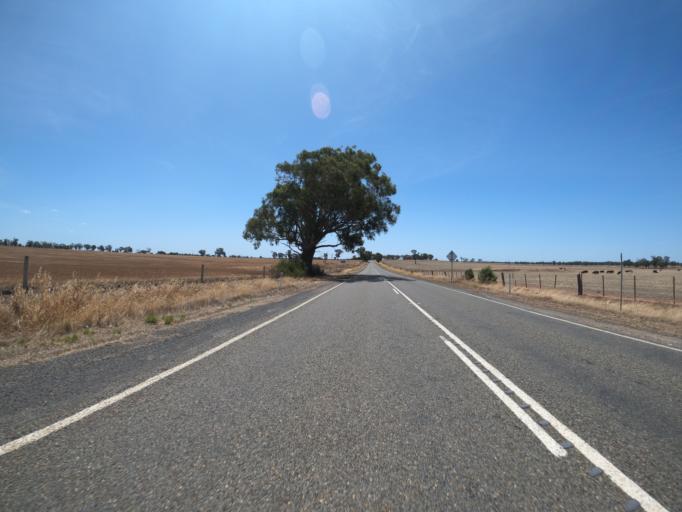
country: AU
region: Victoria
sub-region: Moira
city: Yarrawonga
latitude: -36.0961
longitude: 145.9955
